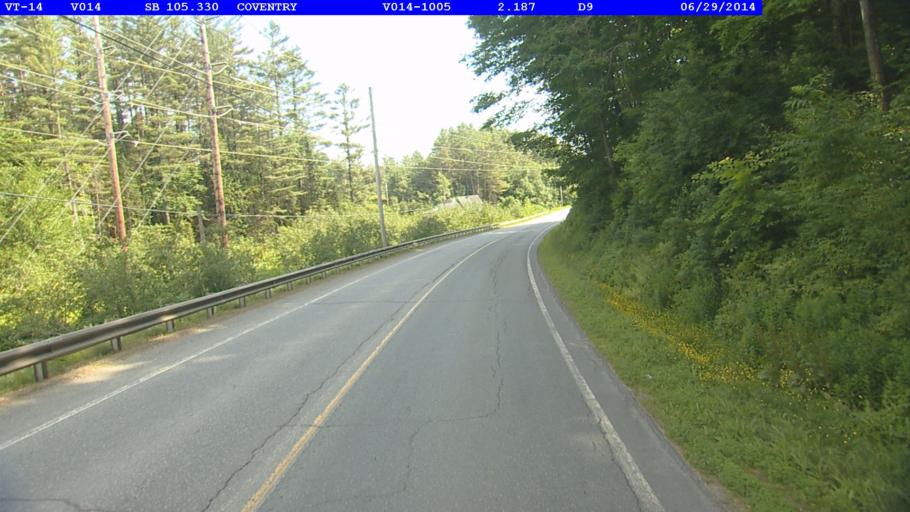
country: US
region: Vermont
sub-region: Orleans County
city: Newport
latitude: 44.8945
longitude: -72.2579
